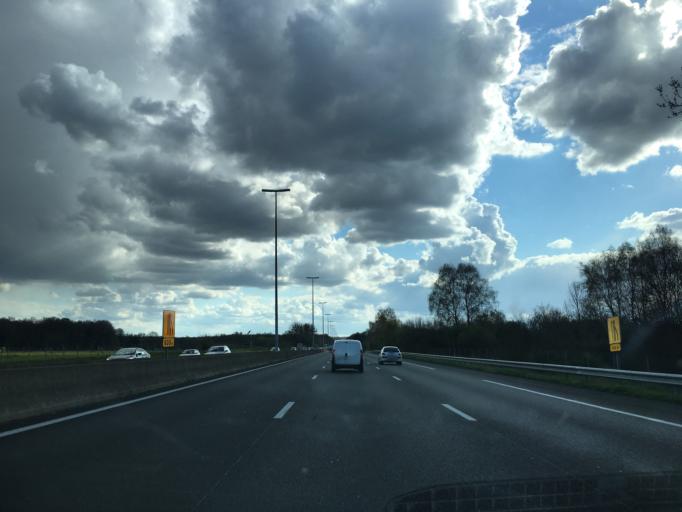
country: FR
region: Picardie
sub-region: Departement de l'Oise
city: Thiers-sur-Theve
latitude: 49.1535
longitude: 2.5872
